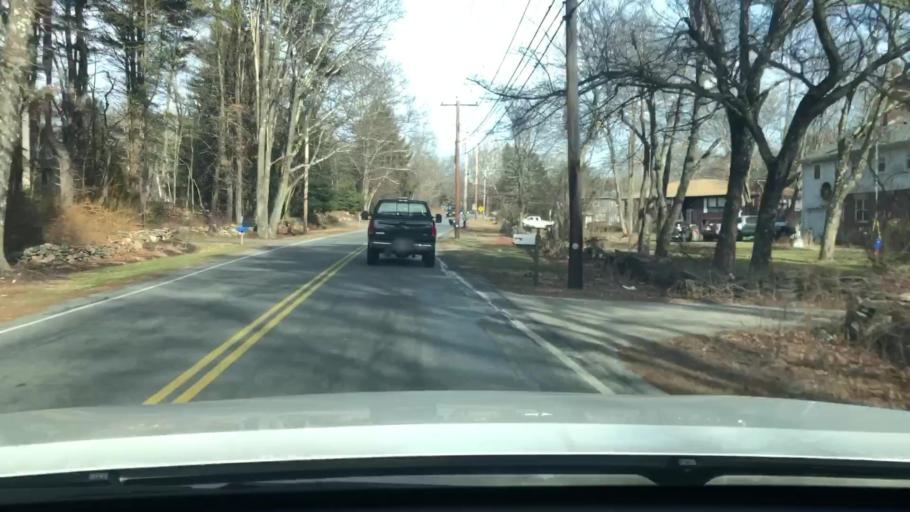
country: US
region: Massachusetts
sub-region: Worcester County
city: Mendon
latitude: 42.0976
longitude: -71.5202
